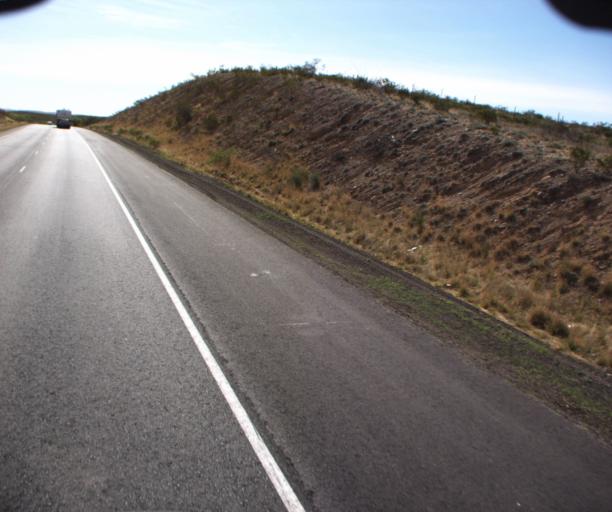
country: US
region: Arizona
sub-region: Pima County
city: Vail
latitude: 31.9888
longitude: -110.5925
